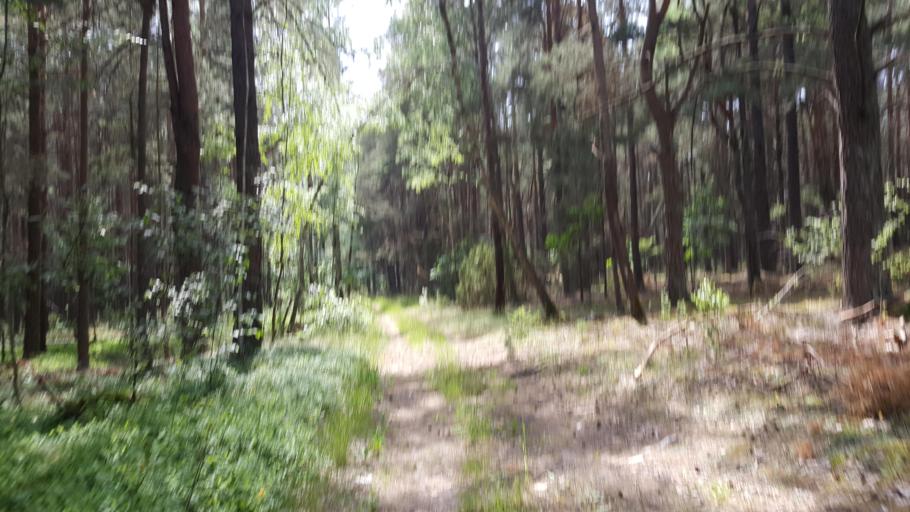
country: BY
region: Brest
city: Kamyanyets
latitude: 52.4793
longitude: 23.8417
